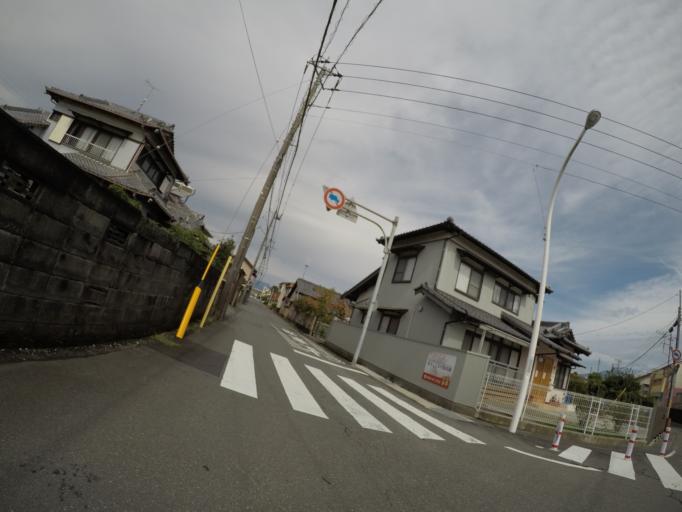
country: JP
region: Shizuoka
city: Fuji
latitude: 35.1383
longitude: 138.6557
